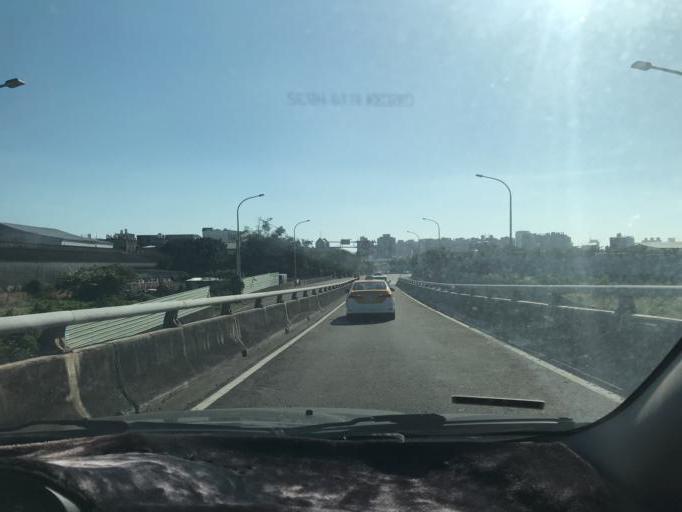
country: TW
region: Taiwan
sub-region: Hsinchu
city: Zhubei
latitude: 24.8195
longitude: 120.9915
